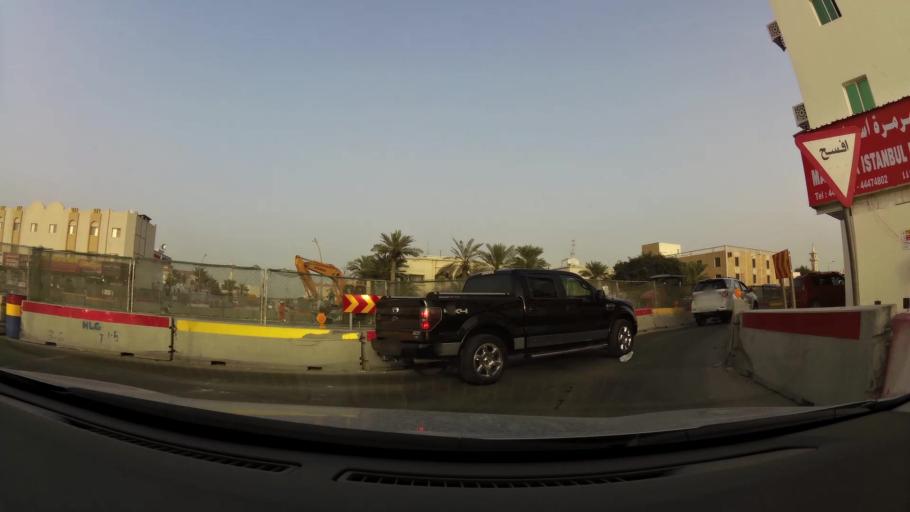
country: QA
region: Baladiyat ar Rayyan
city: Ar Rayyan
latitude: 25.2519
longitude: 51.4506
